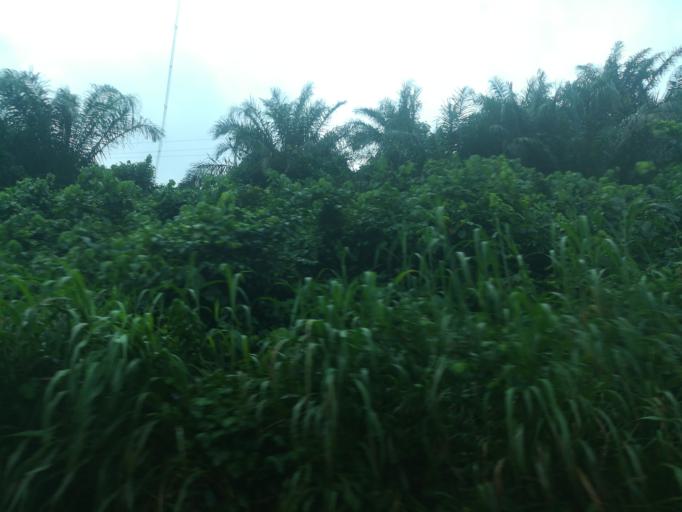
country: NG
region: Lagos
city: Ikorodu
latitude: 6.6637
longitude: 3.6190
